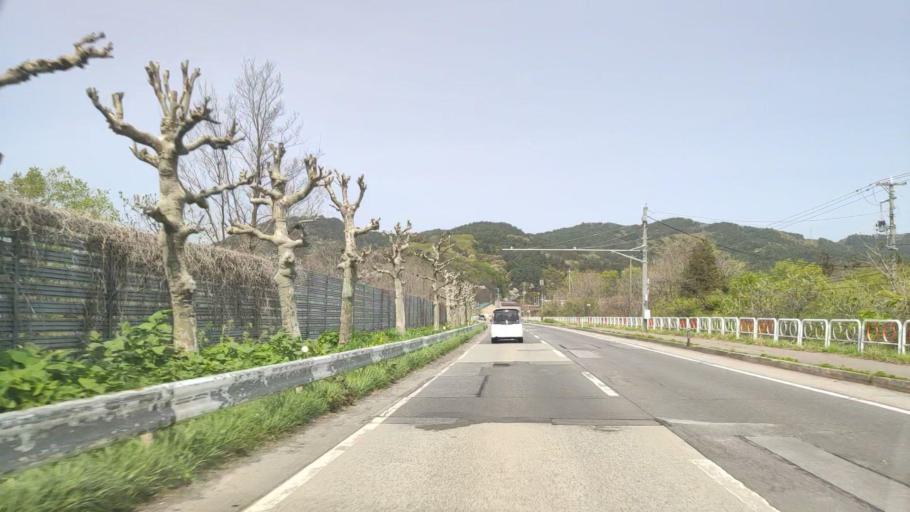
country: JP
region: Aomori
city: Aomori Shi
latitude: 40.8689
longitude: 140.8484
